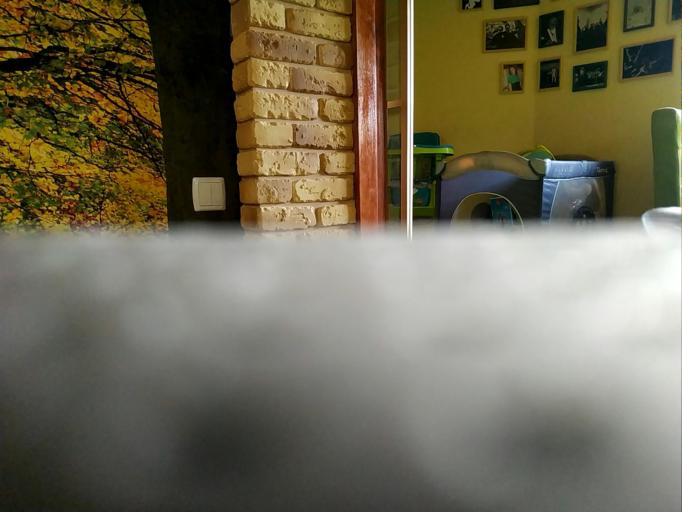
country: RU
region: Kaluga
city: Sukhinichi
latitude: 54.0639
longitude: 35.2932
